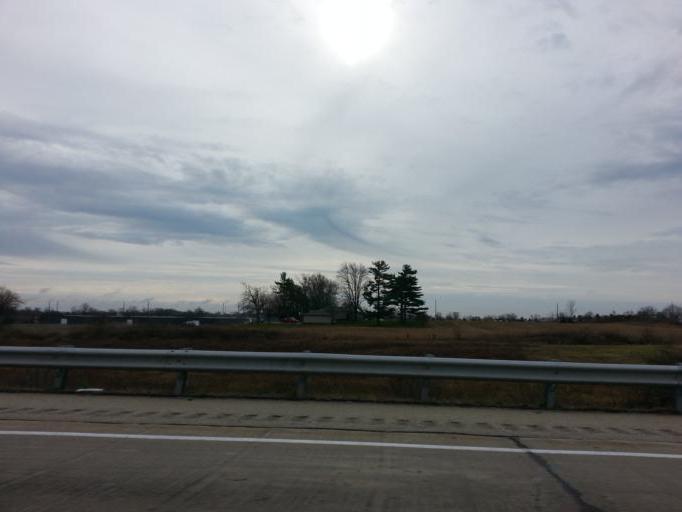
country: US
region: Indiana
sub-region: Decatur County
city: Greensburg
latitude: 39.3622
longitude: -85.4930
